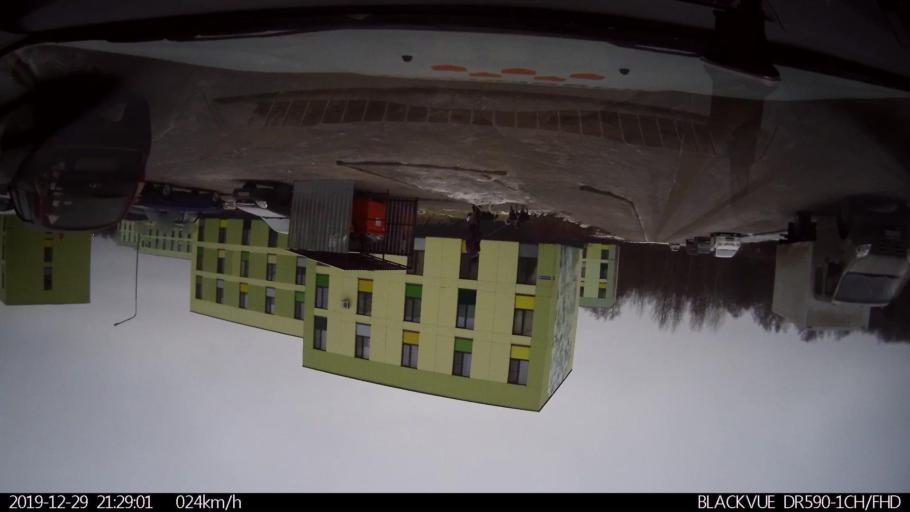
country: RU
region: Nizjnij Novgorod
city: Afonino
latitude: 56.2168
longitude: 44.0177
